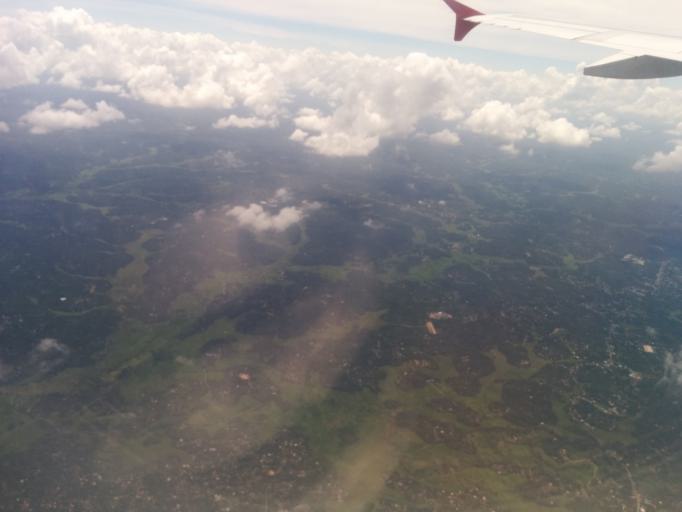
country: LK
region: Western
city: Gampaha
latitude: 7.0744
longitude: 80.0144
